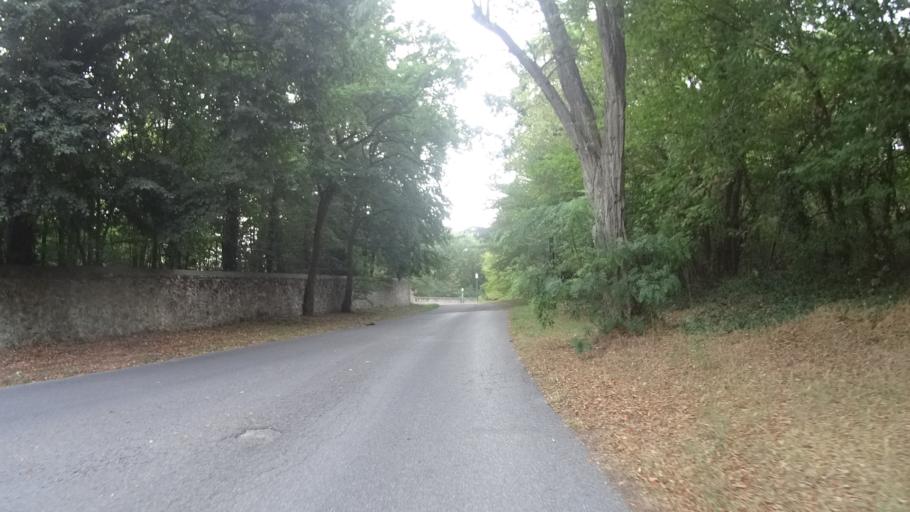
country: FR
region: Picardie
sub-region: Departement de l'Oise
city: Ver-sur-Launette
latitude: 49.1308
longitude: 2.7006
